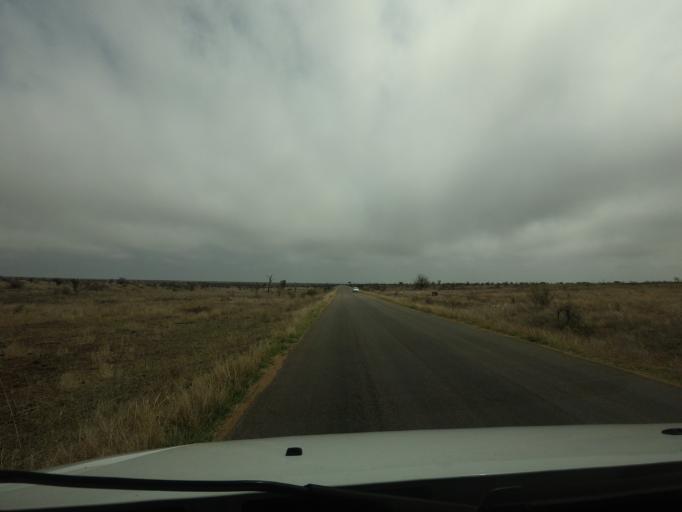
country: ZA
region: Limpopo
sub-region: Mopani District Municipality
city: Phalaborwa
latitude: -24.2081
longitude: 31.7196
